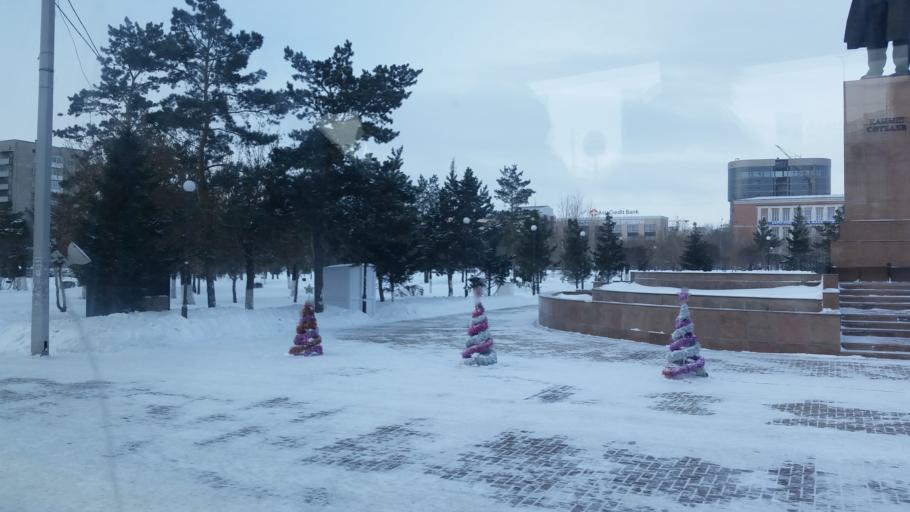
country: KZ
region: Qaraghandy
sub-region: Qaraghandy Qalasy
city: Karagandy
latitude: 49.7940
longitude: 73.0931
